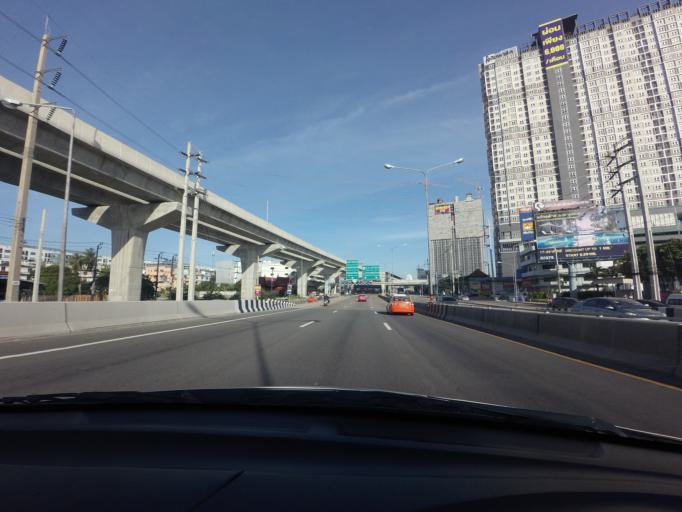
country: TH
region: Nonthaburi
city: Mueang Nonthaburi
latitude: 13.8700
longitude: 100.4705
